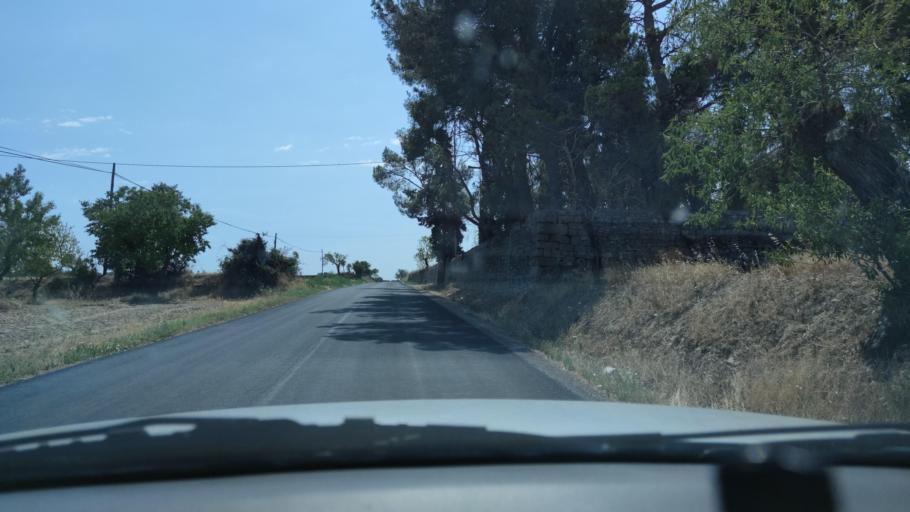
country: ES
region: Catalonia
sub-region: Provincia de Lleida
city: Ivorra
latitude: 41.7813
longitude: 1.3041
